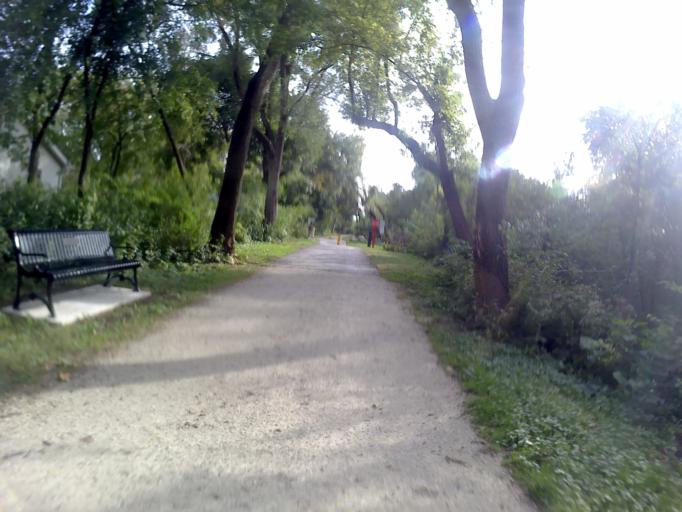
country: US
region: Illinois
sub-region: DuPage County
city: Wheaton
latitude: 41.8565
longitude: -88.1162
